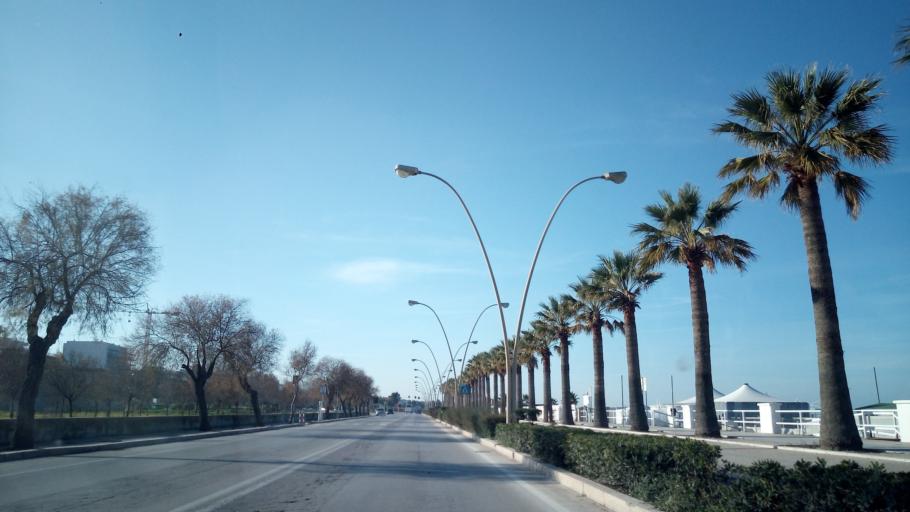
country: IT
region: Apulia
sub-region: Provincia di Barletta - Andria - Trani
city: Barletta
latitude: 41.3233
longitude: 16.2784
